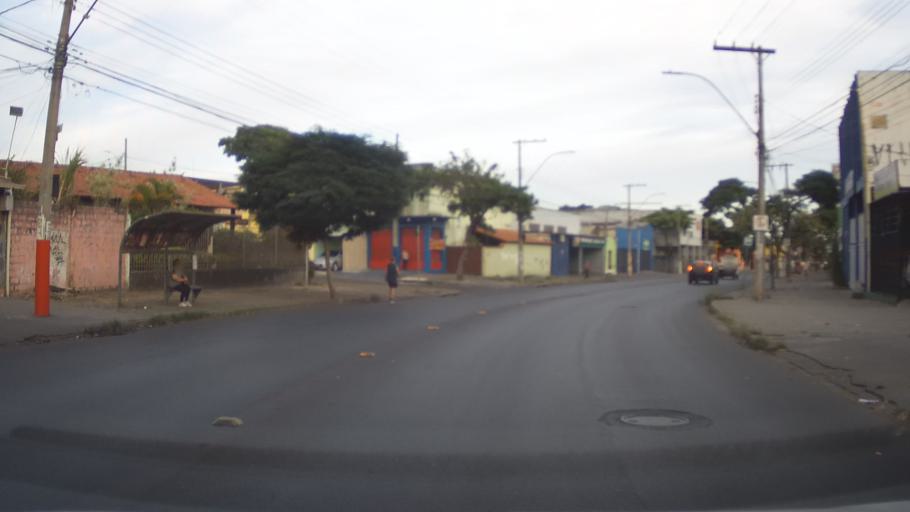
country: BR
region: Minas Gerais
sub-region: Contagem
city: Contagem
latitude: -19.9059
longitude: -44.0056
